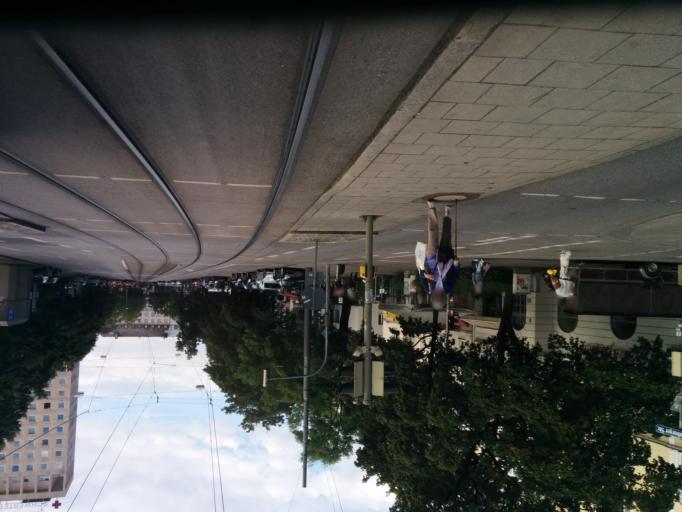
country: DE
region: Bavaria
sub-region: Upper Bavaria
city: Munich
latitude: 48.1551
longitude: 11.5328
